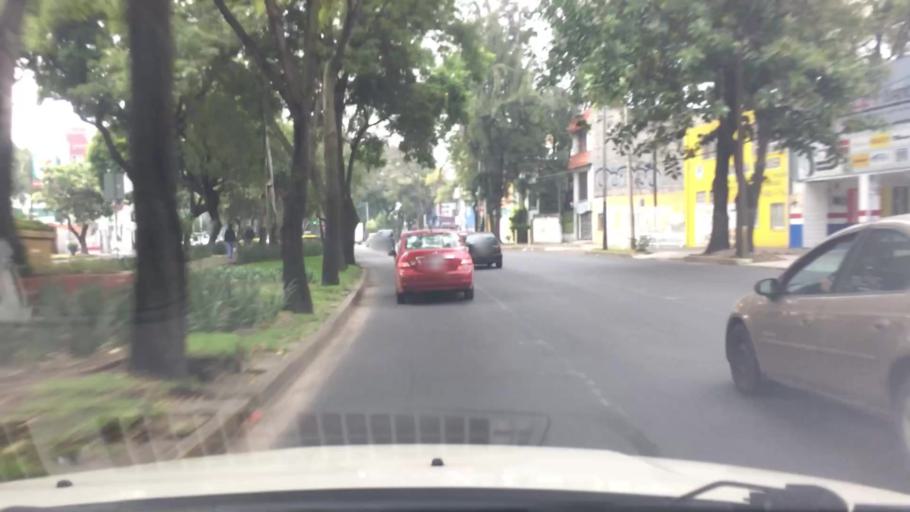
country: MX
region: Mexico City
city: Coyoacan
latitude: 19.3260
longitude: -99.1367
